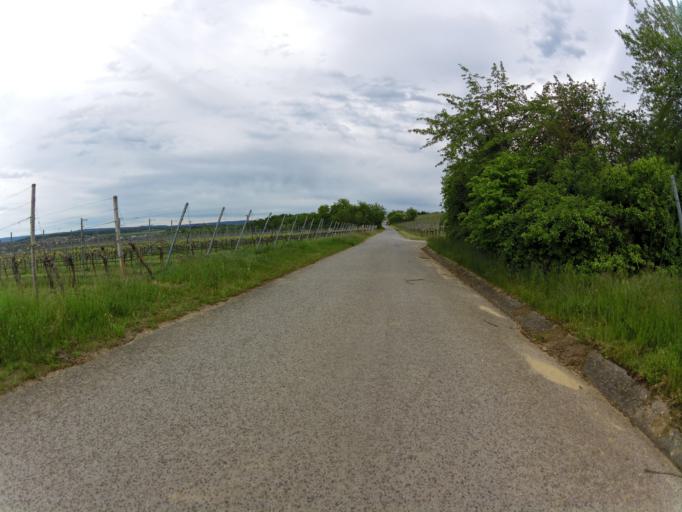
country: DE
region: Bavaria
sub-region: Regierungsbezirk Unterfranken
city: Nordheim
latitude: 49.8537
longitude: 10.1994
